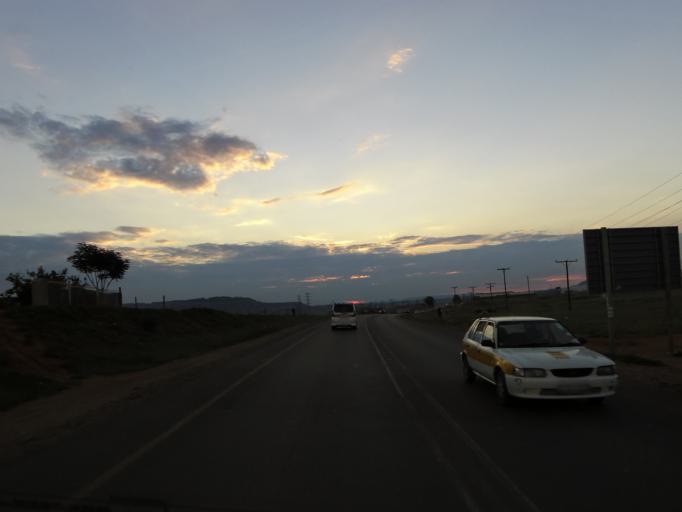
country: LS
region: Leribe
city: Maputsoe
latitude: -28.9135
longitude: 27.9210
